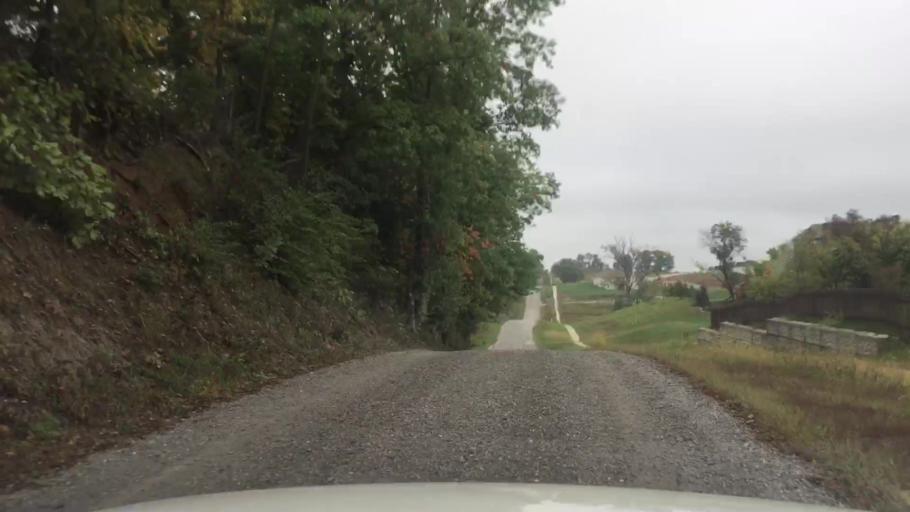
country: US
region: Missouri
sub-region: Boone County
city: Columbia
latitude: 38.8890
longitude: -92.4195
